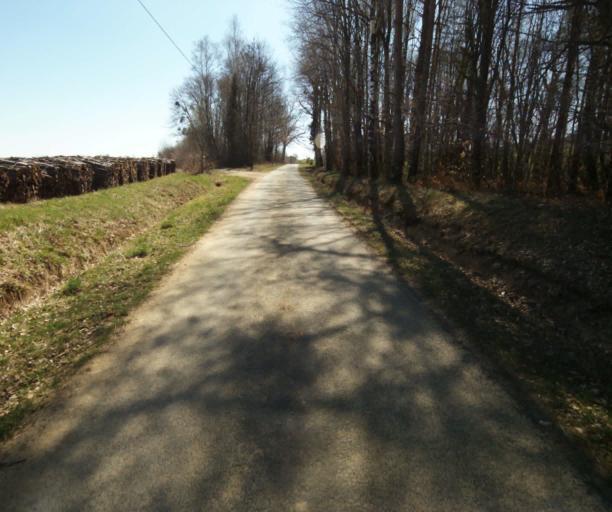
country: FR
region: Limousin
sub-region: Departement de la Correze
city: Saint-Clement
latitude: 45.3159
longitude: 1.6968
